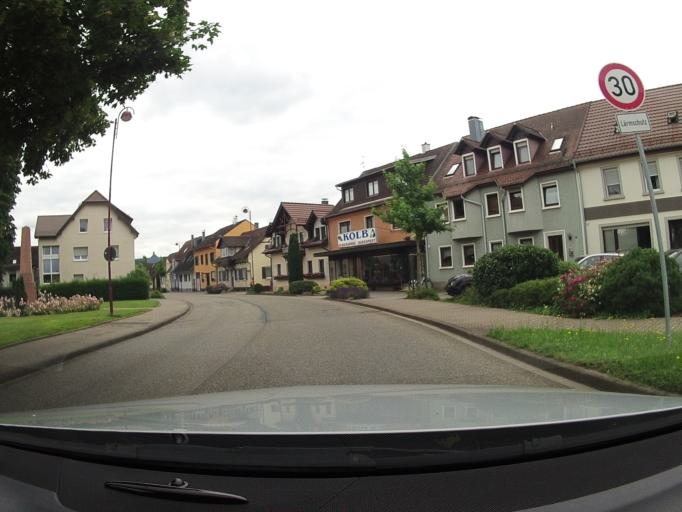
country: DE
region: Baden-Wuerttemberg
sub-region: Karlsruhe Region
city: Kuppenheim
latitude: 48.8322
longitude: 8.2537
